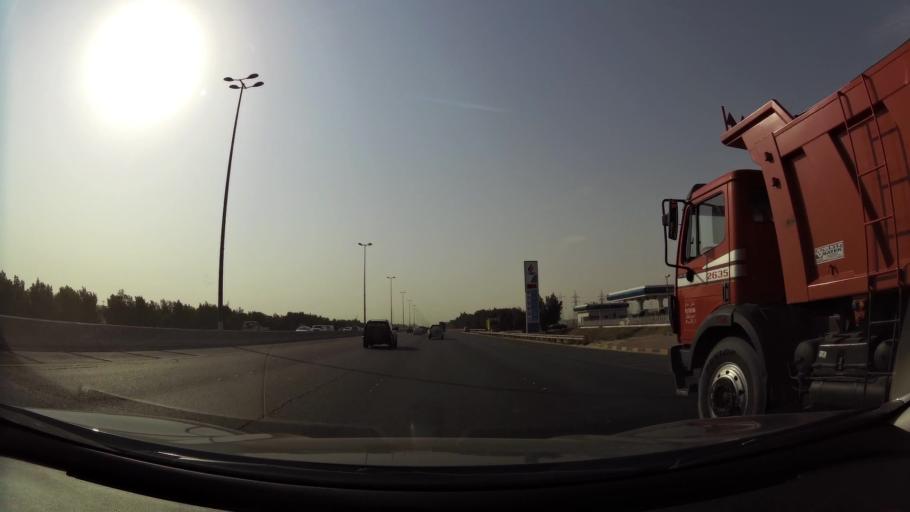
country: KW
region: Al Ahmadi
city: Ar Riqqah
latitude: 29.1154
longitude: 48.0942
